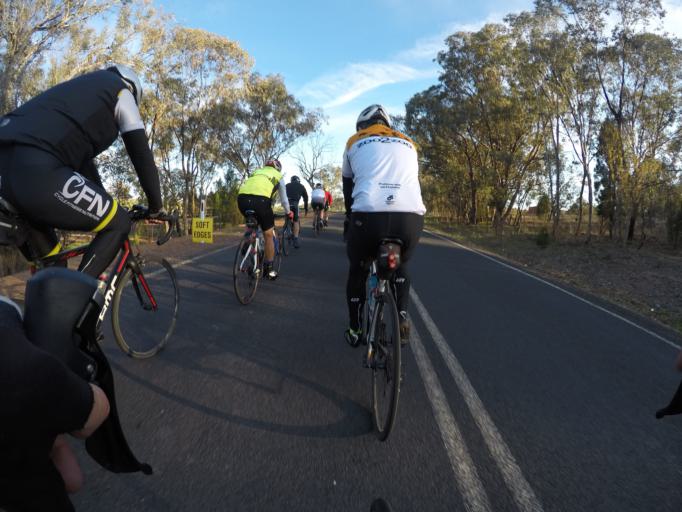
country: AU
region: New South Wales
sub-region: Cabonne
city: Molong
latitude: -33.0691
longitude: 148.8253
